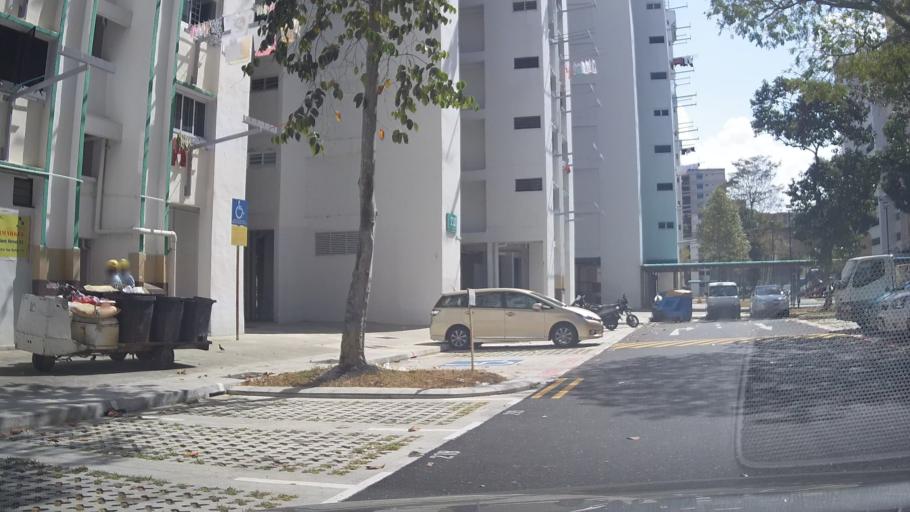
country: SG
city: Singapore
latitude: 1.3562
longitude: 103.9474
